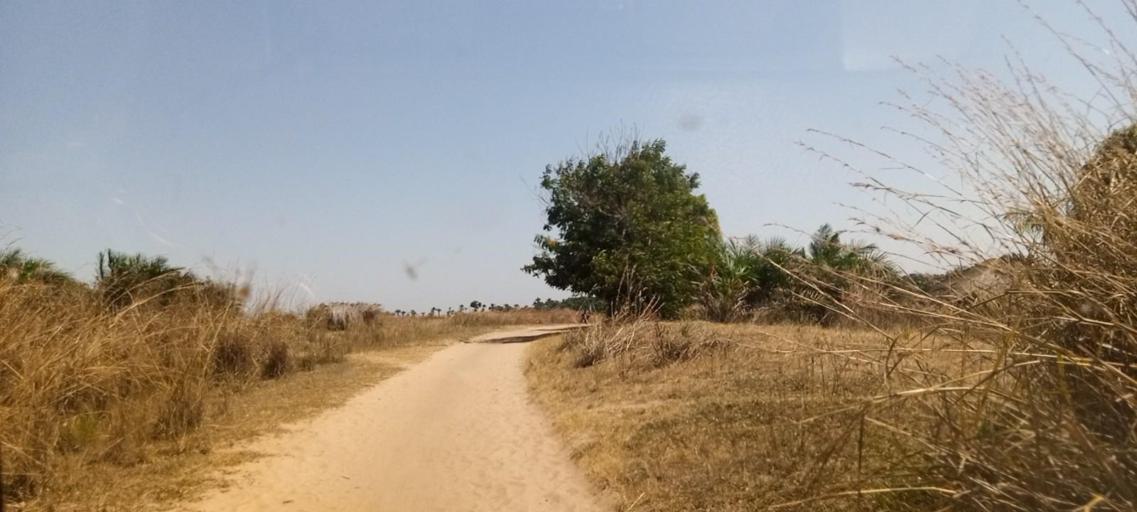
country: CD
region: Kasai-Oriental
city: Kabinda
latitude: -5.9618
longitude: 24.7843
